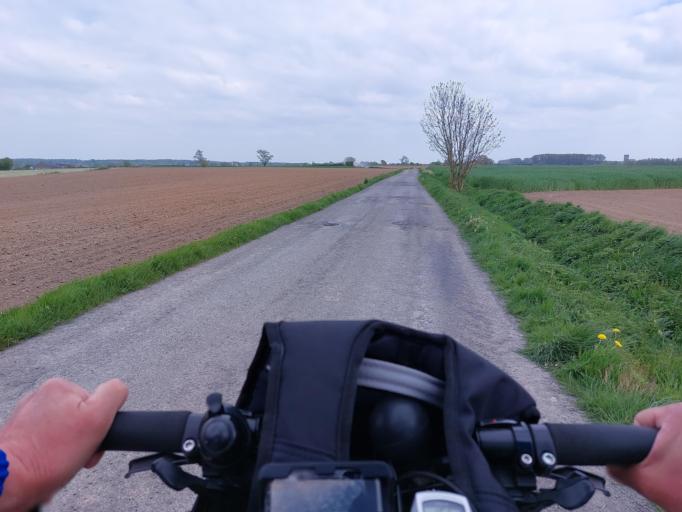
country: FR
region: Nord-Pas-de-Calais
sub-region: Departement du Nord
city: Bavay
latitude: 50.2933
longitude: 3.8205
